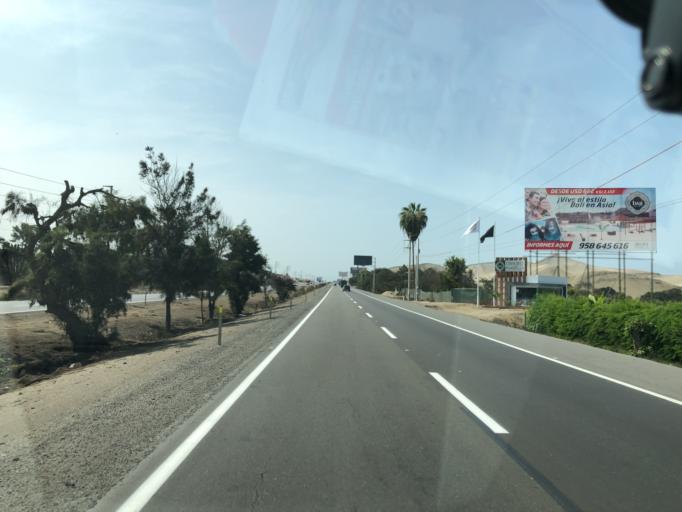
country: PE
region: Lima
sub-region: Provincia de Canete
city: Mala
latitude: -12.7284
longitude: -76.6163
